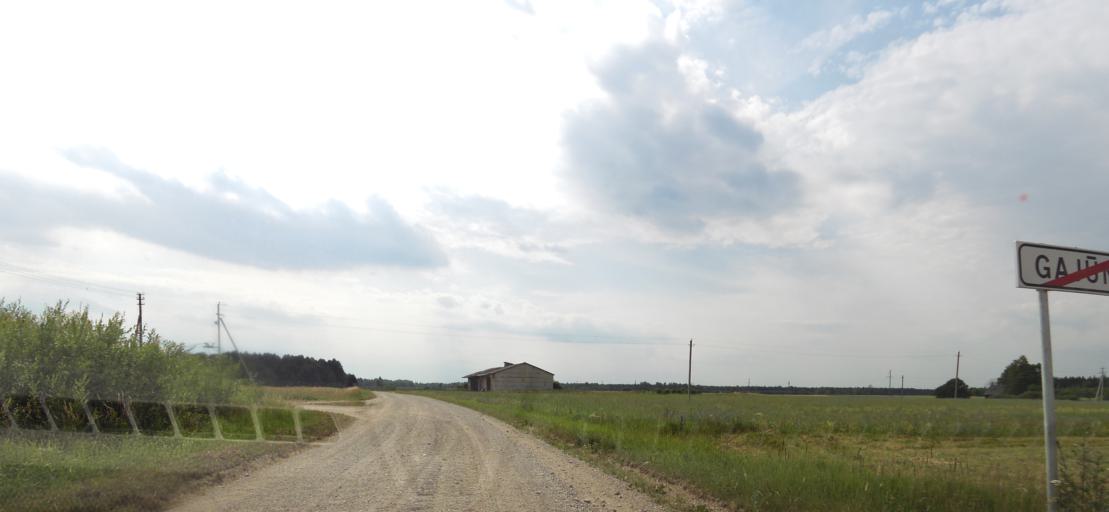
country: LT
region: Panevezys
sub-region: Birzai
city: Birzai
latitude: 56.1847
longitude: 24.9845
